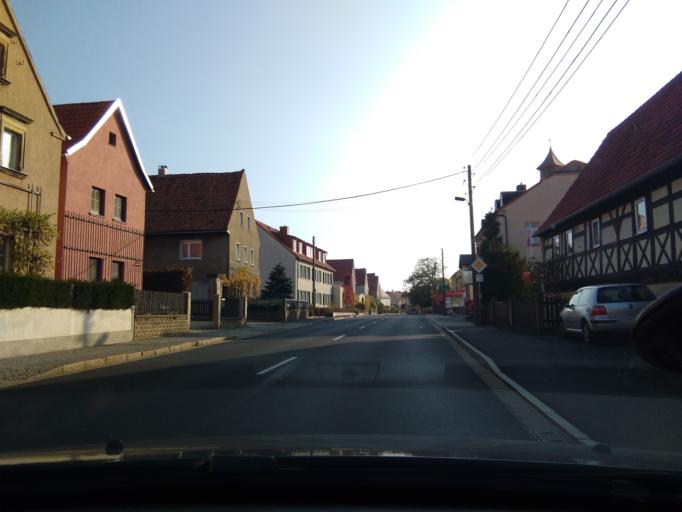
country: DE
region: Saxony
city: Niederau
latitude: 51.1371
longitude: 13.5186
